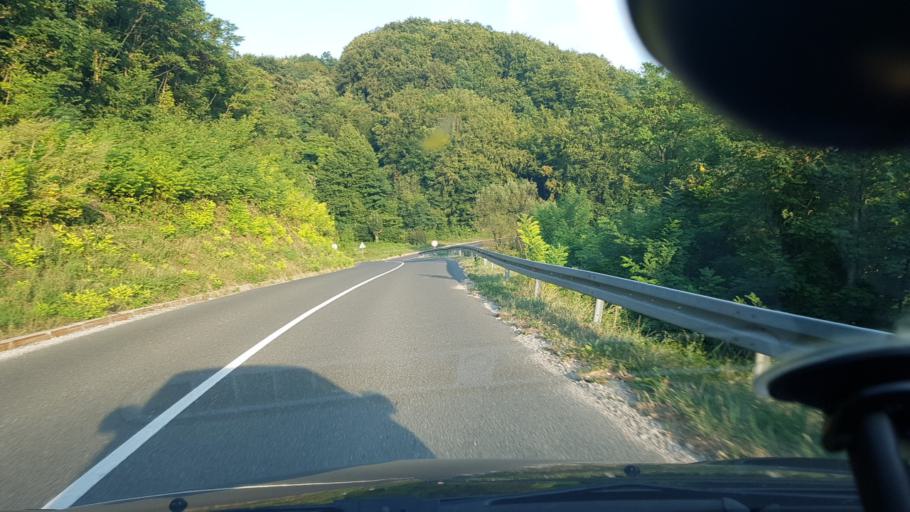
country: HR
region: Krapinsko-Zagorska
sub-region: Grad Krapina
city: Krapina
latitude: 46.1692
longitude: 15.8485
